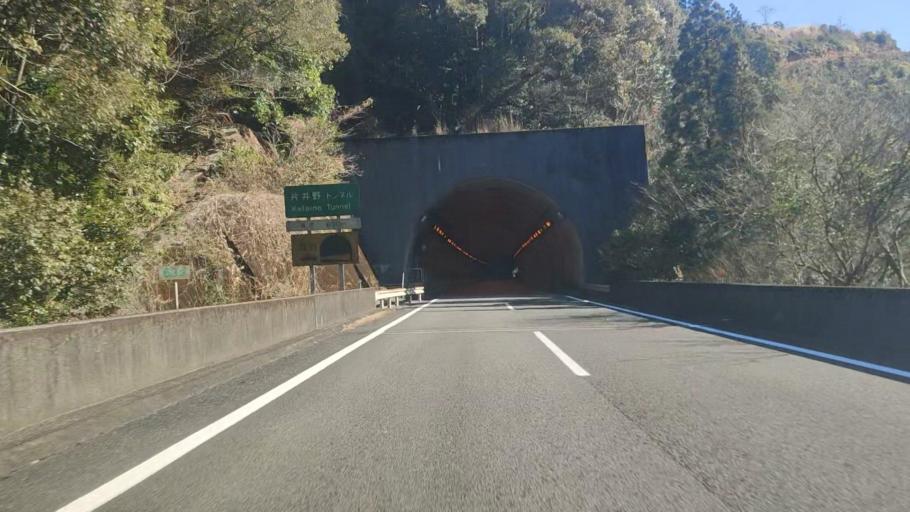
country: JP
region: Miyazaki
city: Miyazaki-shi
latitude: 31.8213
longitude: 131.2559
